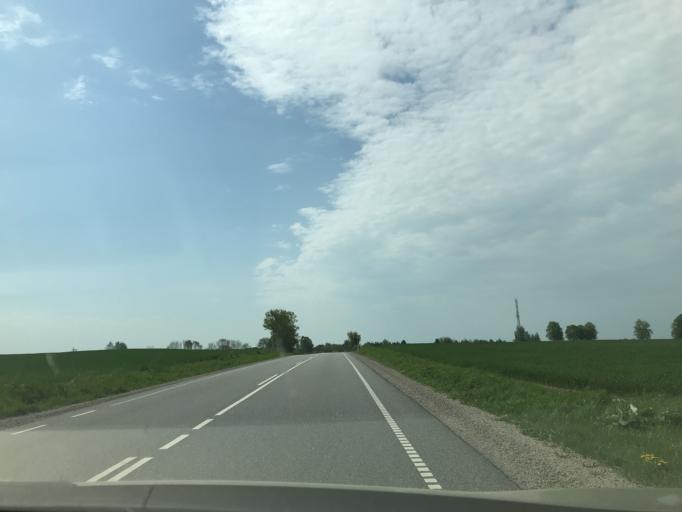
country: DK
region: South Denmark
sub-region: Middelfart Kommune
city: Ejby
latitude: 55.3815
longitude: 9.9176
